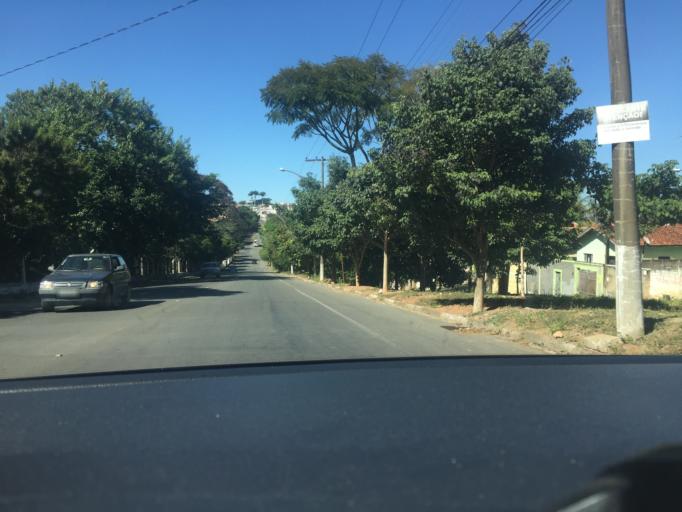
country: BR
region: Sao Paulo
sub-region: Santo Antonio Do Jardim
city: Espirito Santo do Pinhal
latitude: -22.1779
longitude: -46.7455
